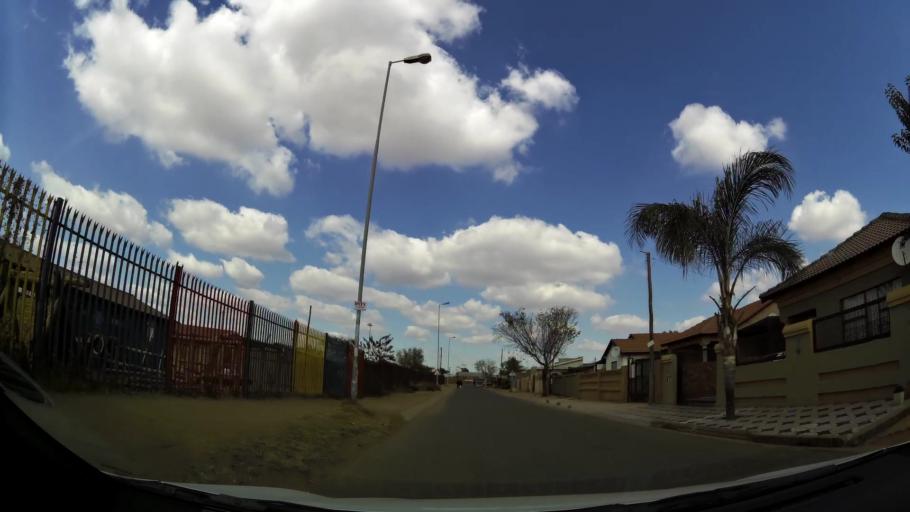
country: ZA
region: Gauteng
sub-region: City of Tshwane Metropolitan Municipality
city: Cullinan
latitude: -25.7034
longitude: 28.3982
